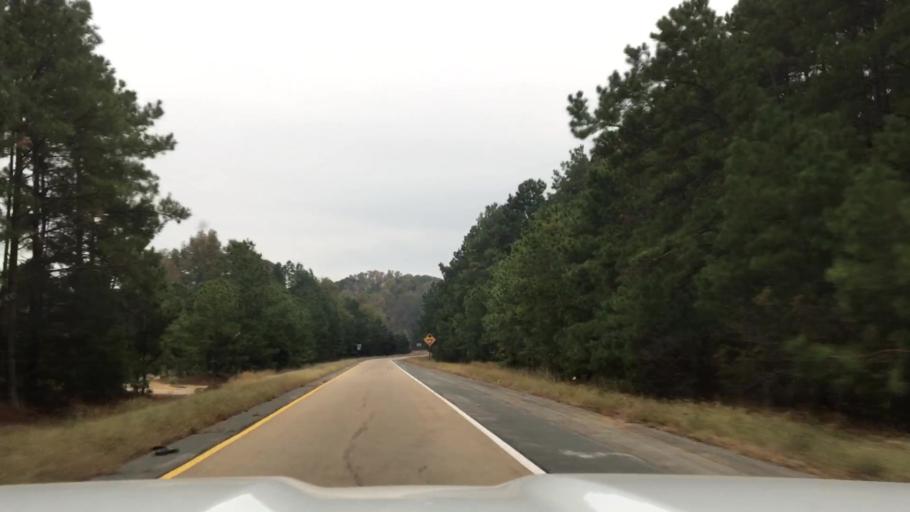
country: US
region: Virginia
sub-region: Hanover County
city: Mechanicsville
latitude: 37.6090
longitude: -77.3637
